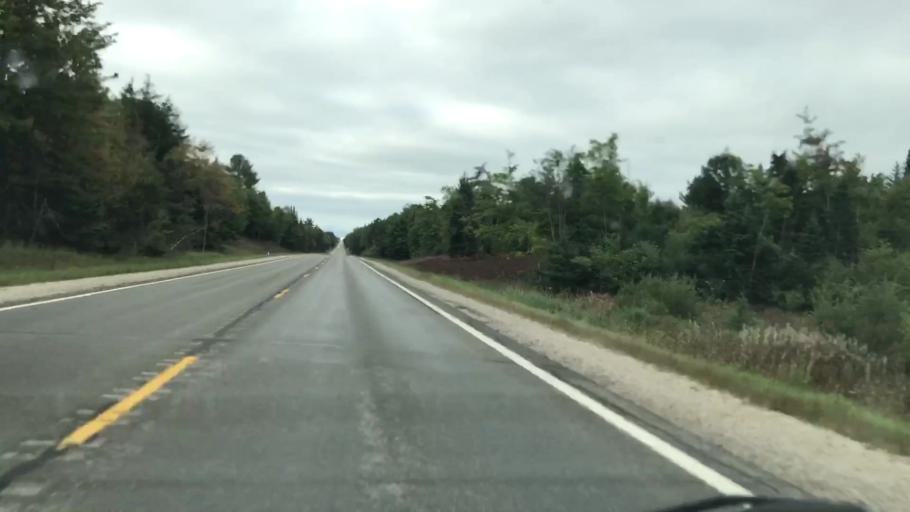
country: US
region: Michigan
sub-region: Luce County
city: Newberry
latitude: 46.2395
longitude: -85.5722
